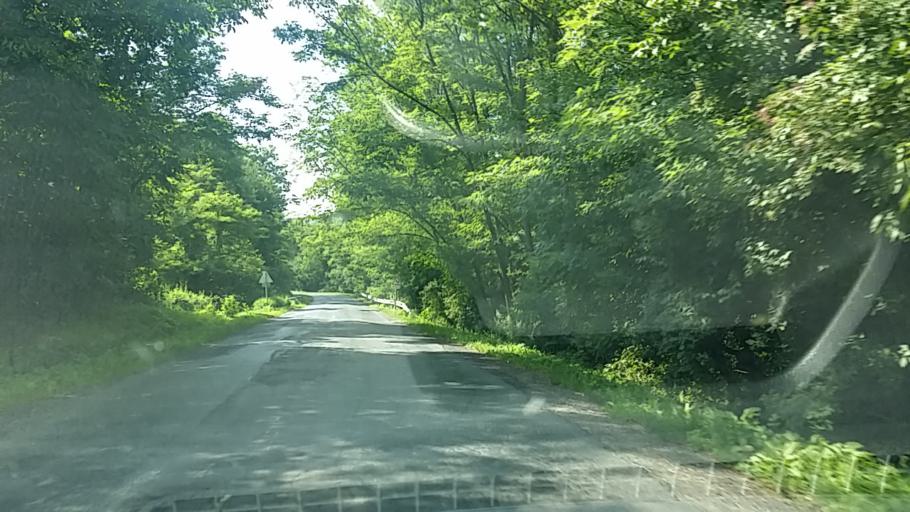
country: HU
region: Zala
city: Becsehely
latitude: 46.5221
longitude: 16.7686
